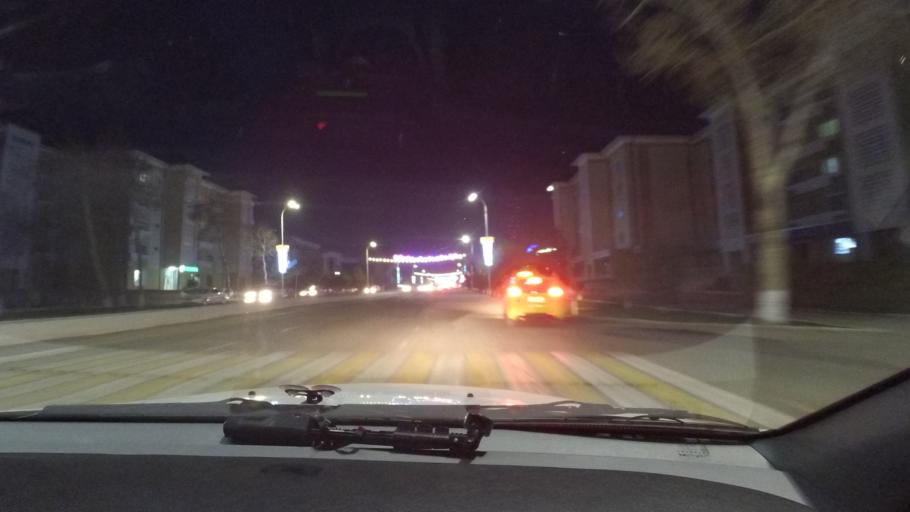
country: UZ
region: Bukhara
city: Bukhara
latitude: 39.7706
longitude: 64.4469
